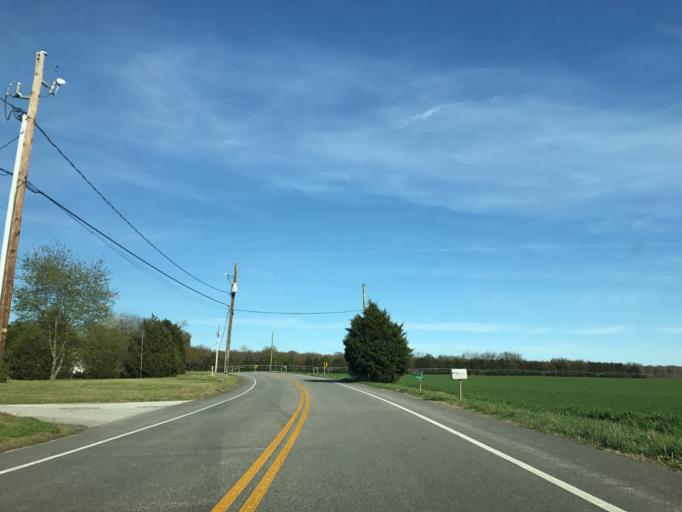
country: US
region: Maryland
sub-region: Caroline County
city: Greensboro
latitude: 39.0290
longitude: -75.7536
